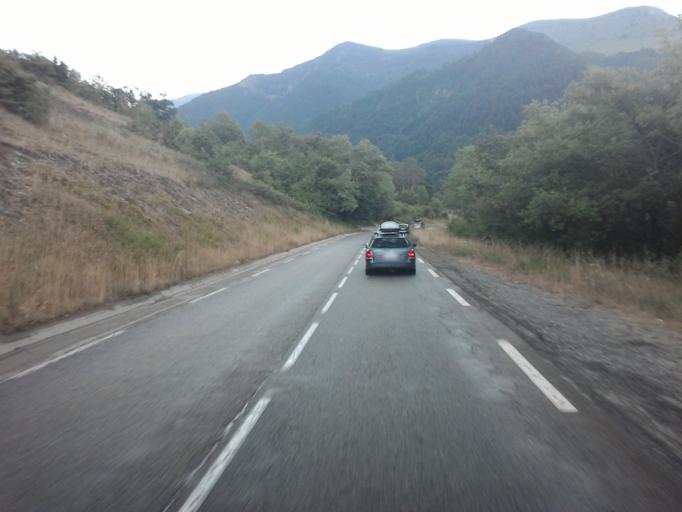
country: FR
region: Rhone-Alpes
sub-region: Departement de l'Isere
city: La Mure
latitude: 44.8244
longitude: 5.9427
